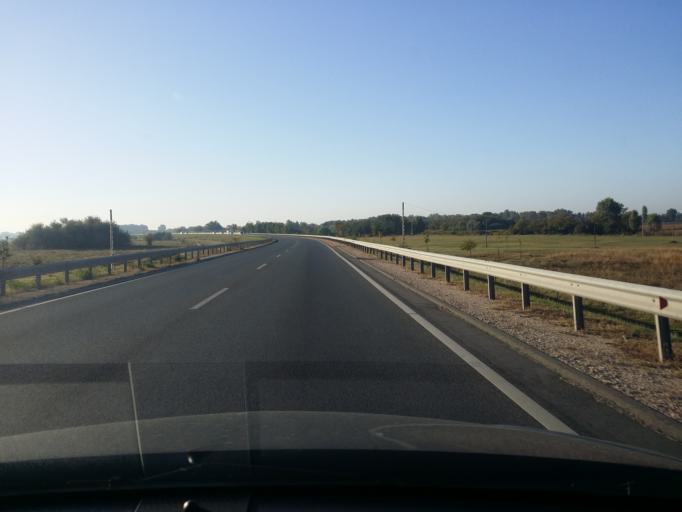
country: HU
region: Bacs-Kiskun
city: Kecskemet
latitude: 46.9311
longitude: 19.7144
